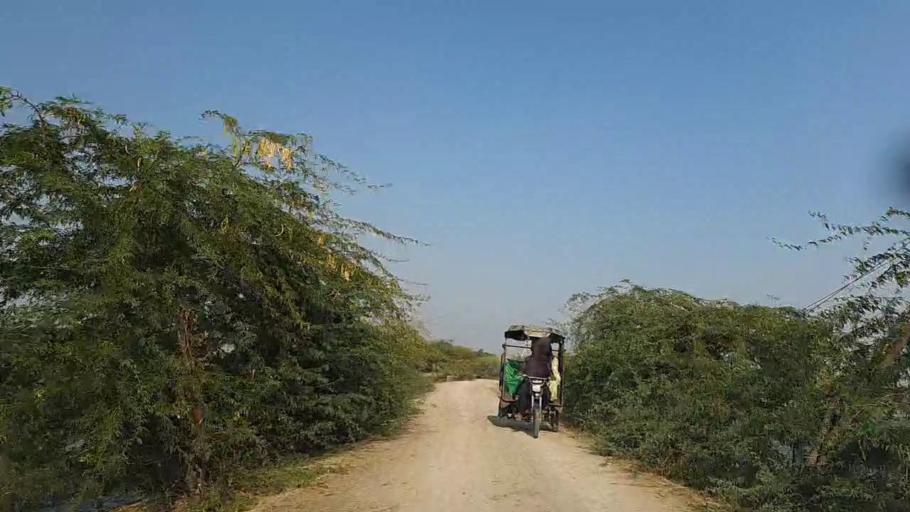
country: PK
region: Sindh
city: Jati
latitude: 24.5235
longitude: 68.2648
